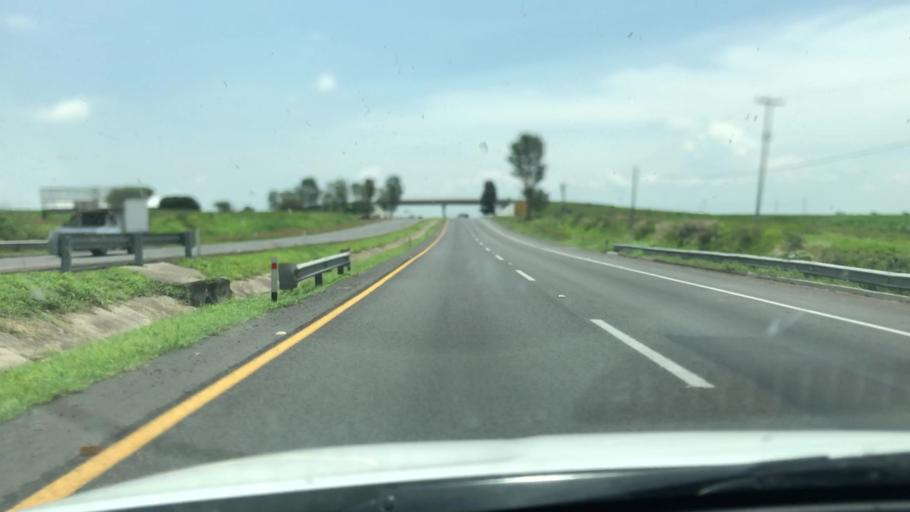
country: MX
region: Guanajuato
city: Penjamo
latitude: 20.3846
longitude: -101.7883
